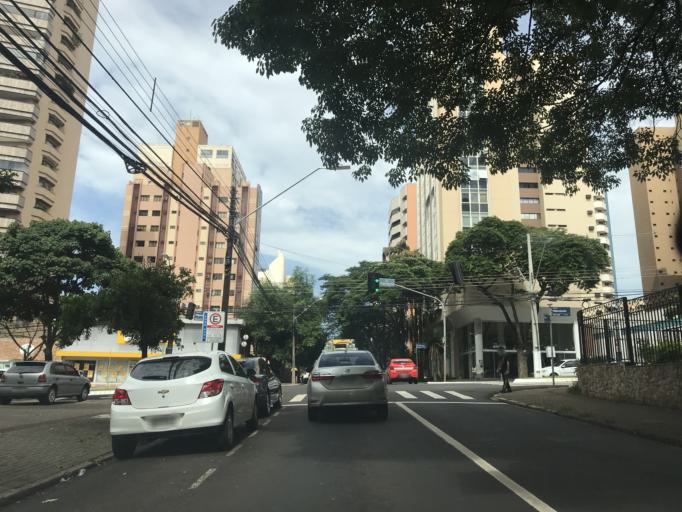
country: BR
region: Parana
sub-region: Londrina
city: Londrina
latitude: -23.3145
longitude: -51.1651
